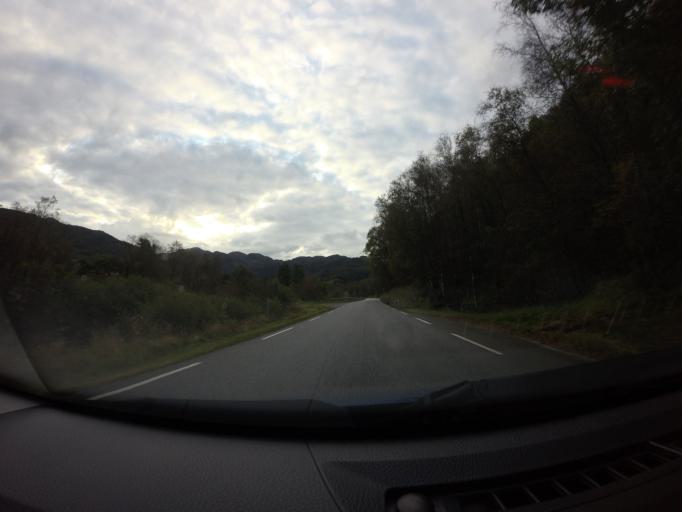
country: NO
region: Rogaland
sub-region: Forsand
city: Forsand
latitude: 58.8038
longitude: 6.2575
